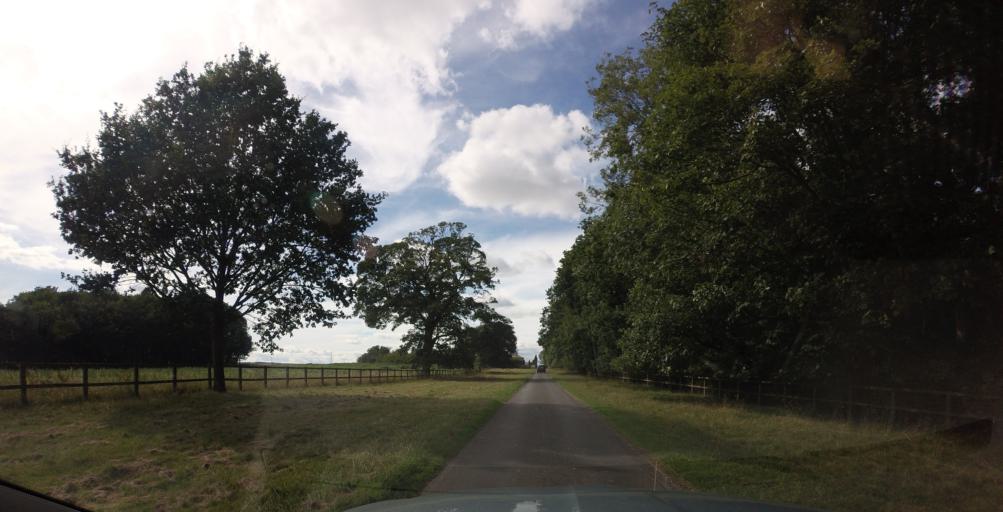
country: GB
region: England
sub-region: North Yorkshire
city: Ripon
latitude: 54.1092
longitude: -1.4729
